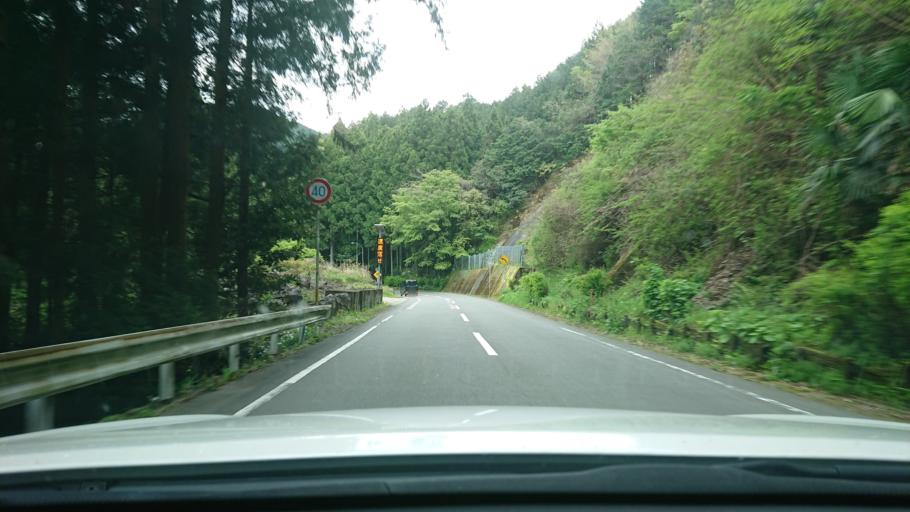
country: JP
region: Tokushima
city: Ishii
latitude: 33.9160
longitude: 134.4241
